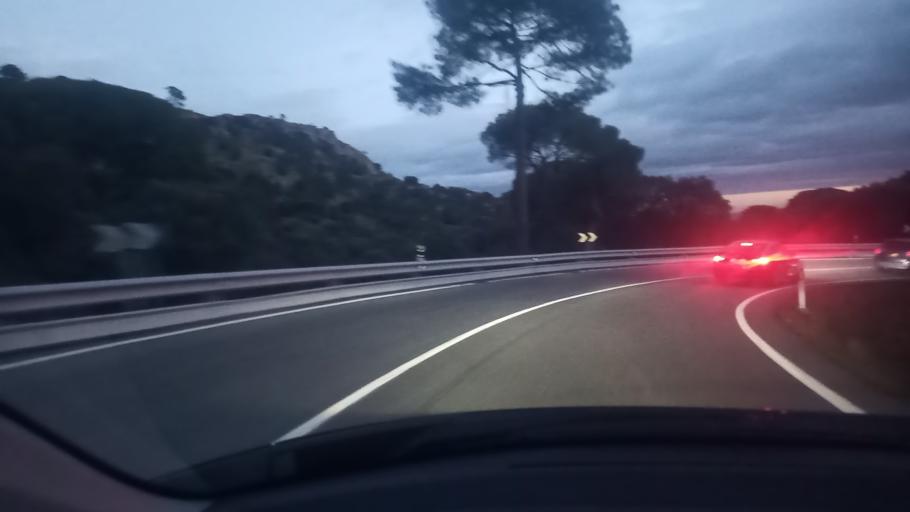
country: ES
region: Madrid
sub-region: Provincia de Madrid
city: Navas del Rey
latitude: 40.4408
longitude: -4.2664
